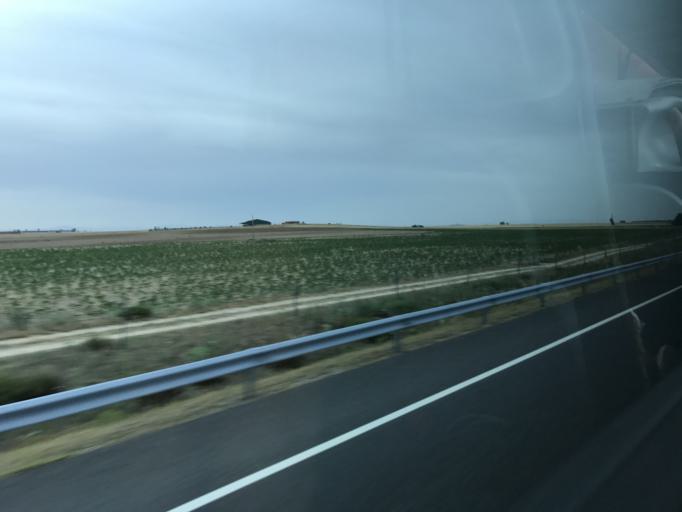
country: ES
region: Castille and Leon
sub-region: Provincia de Segovia
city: San Cristobal de la Vega
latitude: 41.1019
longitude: -4.6394
